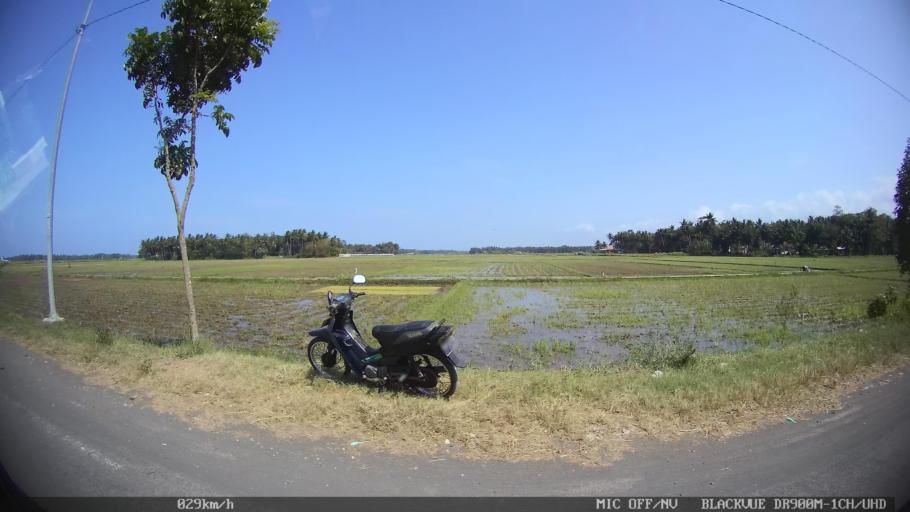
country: ID
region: Daerah Istimewa Yogyakarta
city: Srandakan
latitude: -7.9622
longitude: 110.2146
